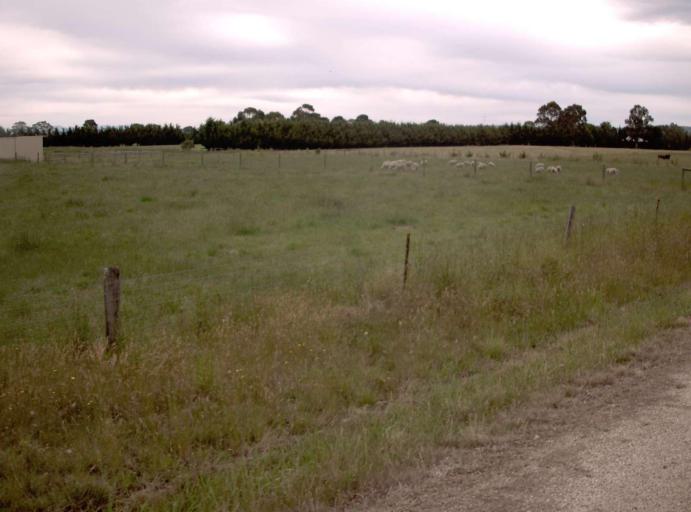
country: AU
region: Victoria
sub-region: East Gippsland
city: Bairnsdale
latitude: -37.8687
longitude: 147.5616
